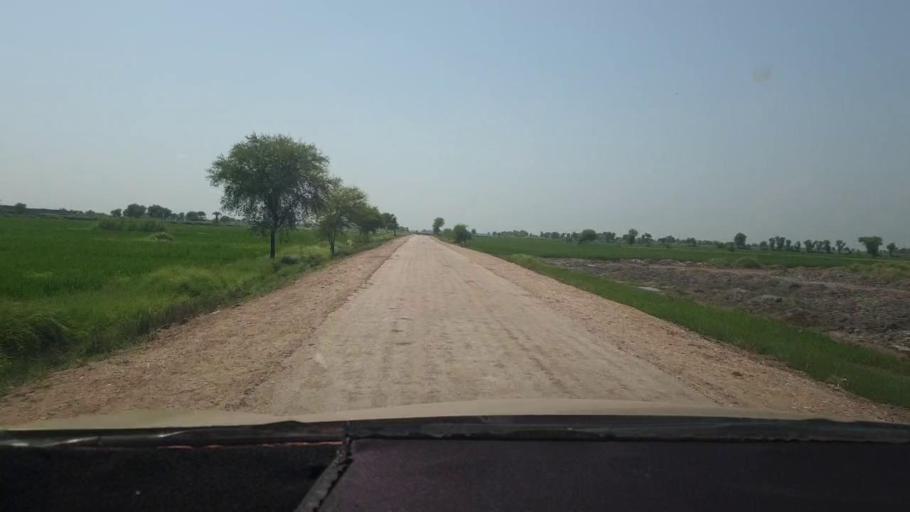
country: PK
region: Sindh
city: Miro Khan
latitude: 27.6665
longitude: 68.0952
